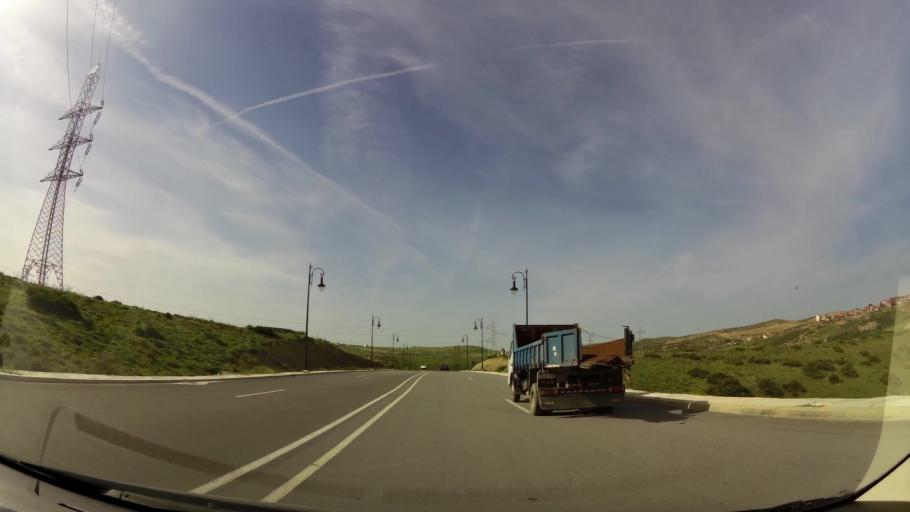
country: MA
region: Tanger-Tetouan
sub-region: Tanger-Assilah
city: Tangier
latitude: 35.7171
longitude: -5.7730
